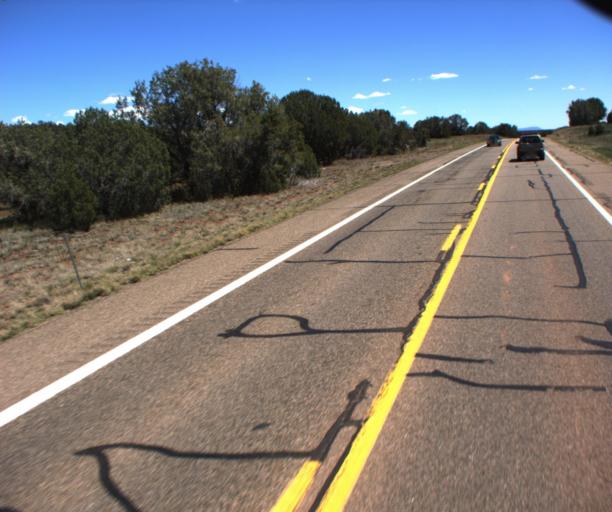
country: US
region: Arizona
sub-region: Yavapai County
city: Paulden
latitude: 35.1387
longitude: -112.4425
